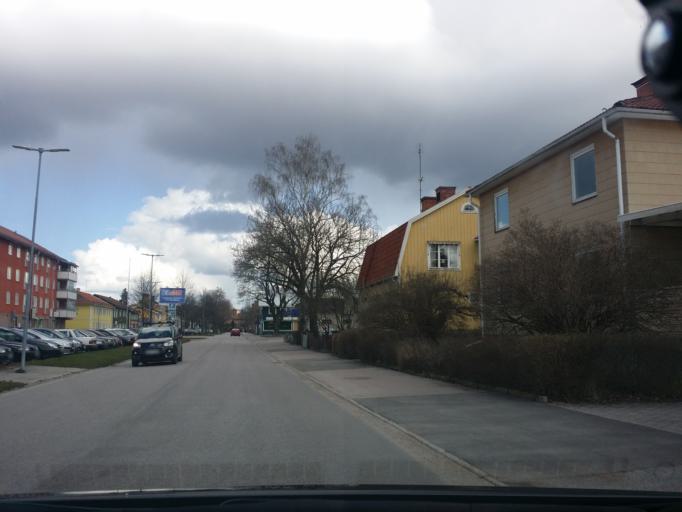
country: SE
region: Vaestmanland
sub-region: Sala Kommun
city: Sala
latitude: 59.9176
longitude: 16.6108
